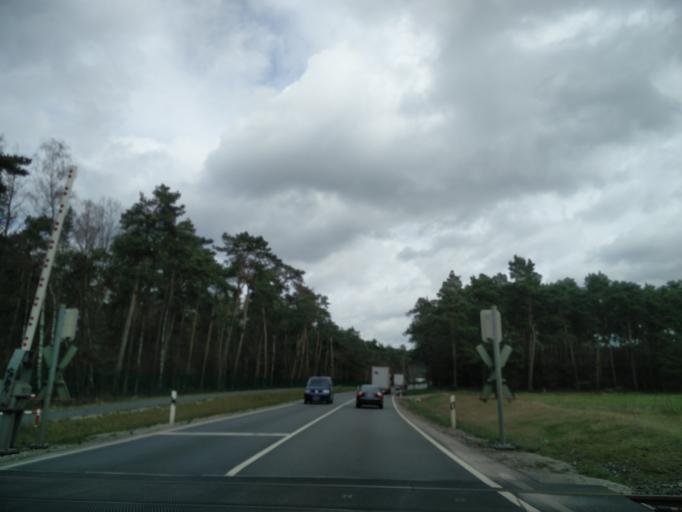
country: DE
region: North Rhine-Westphalia
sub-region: Regierungsbezirk Detmold
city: Steinhagen
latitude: 52.0290
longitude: 8.3952
